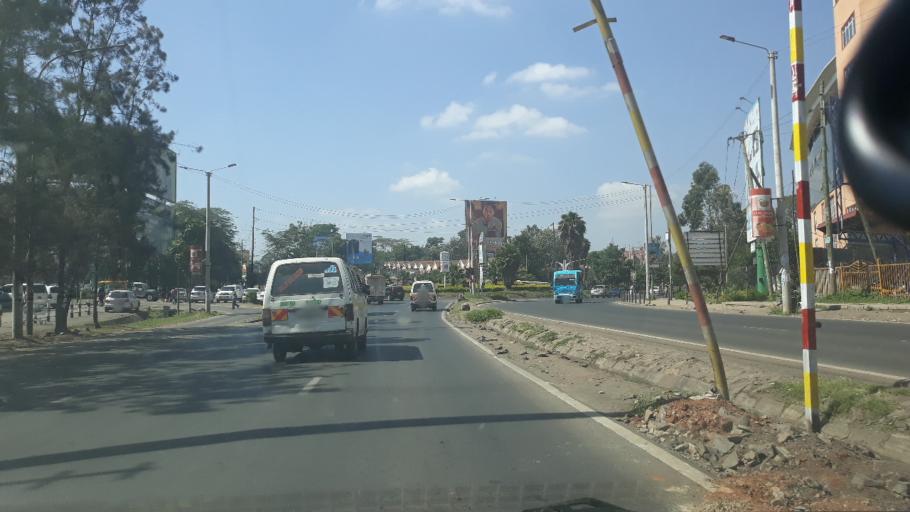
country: KE
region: Nairobi Area
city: Nairobi
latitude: -1.3119
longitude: 36.8165
